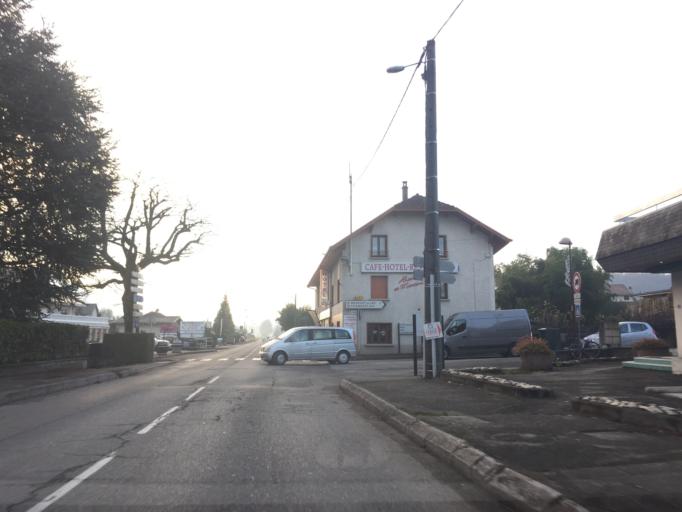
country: FR
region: Rhone-Alpes
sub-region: Departement de la Savoie
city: Viviers-du-Lac
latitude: 45.6490
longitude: 5.9092
